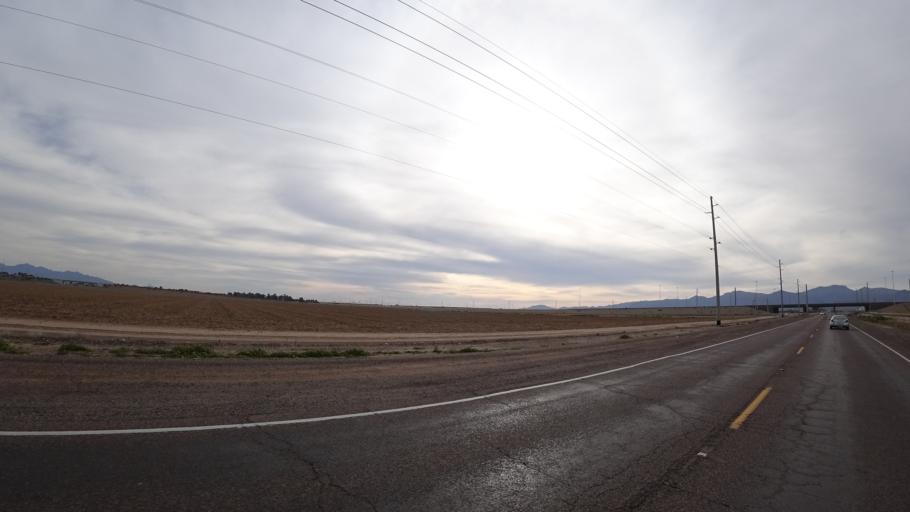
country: US
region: Arizona
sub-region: Maricopa County
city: Citrus Park
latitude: 33.5662
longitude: -112.4117
